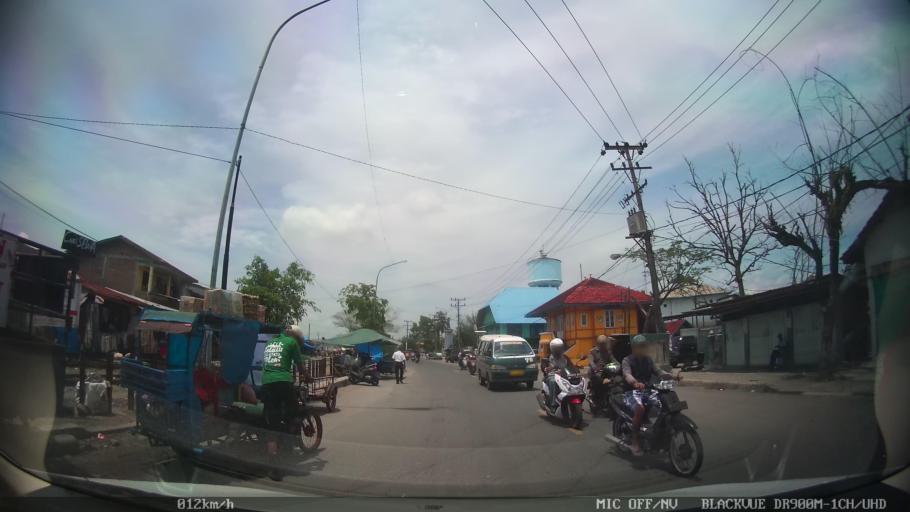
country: ID
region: North Sumatra
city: Belawan
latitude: 3.7826
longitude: 98.6835
